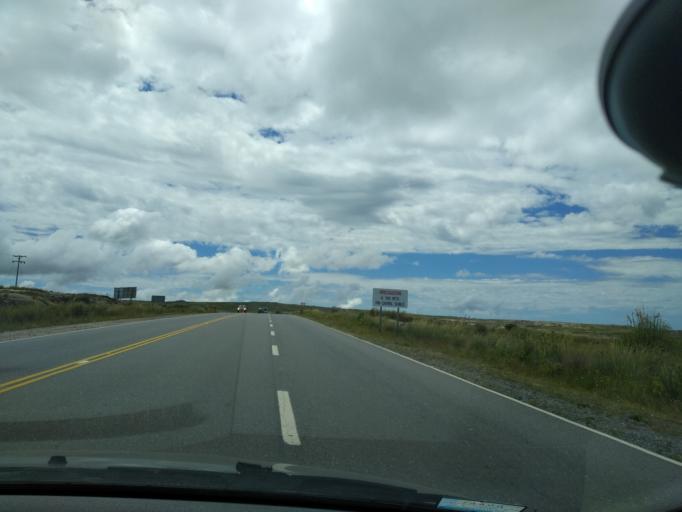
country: AR
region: Cordoba
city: Mina Clavero
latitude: -31.6175
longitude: -64.8723
